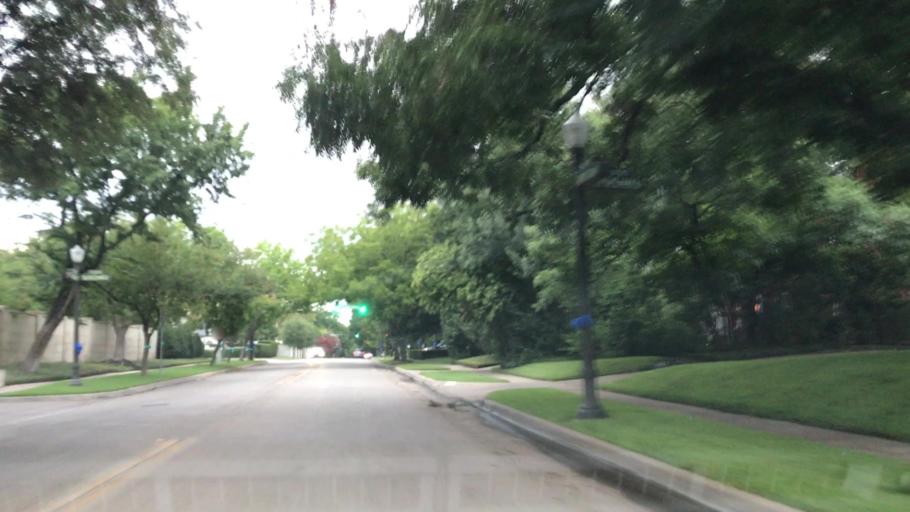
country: US
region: Texas
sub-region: Dallas County
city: University Park
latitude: 32.8511
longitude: -96.7940
